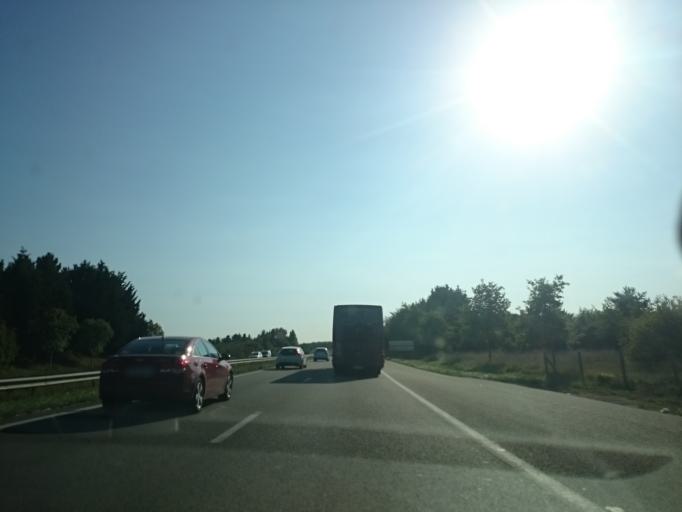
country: FR
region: Pays de la Loire
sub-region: Departement de la Loire-Atlantique
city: Bouguenais
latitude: 47.1689
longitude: -1.6193
